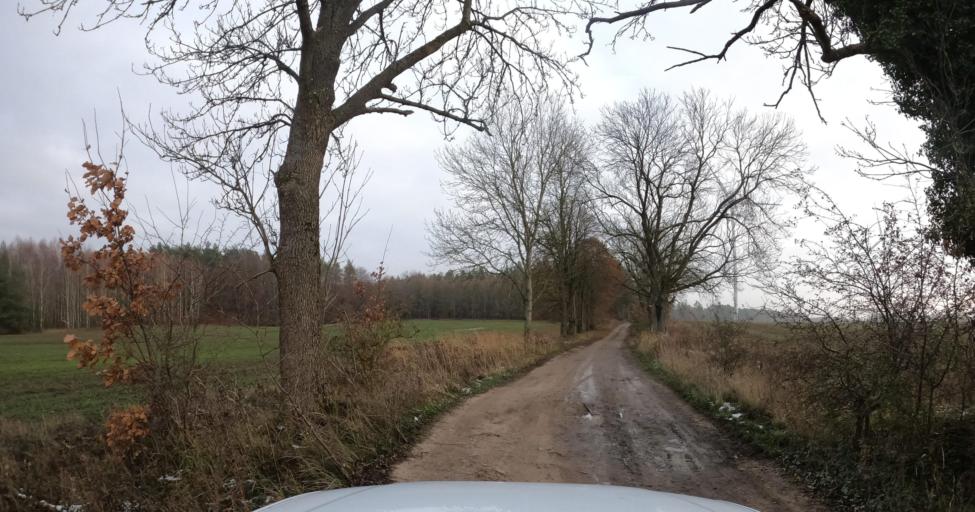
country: PL
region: West Pomeranian Voivodeship
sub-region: Powiat bialogardzki
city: Karlino
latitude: 53.9274
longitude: 15.8340
